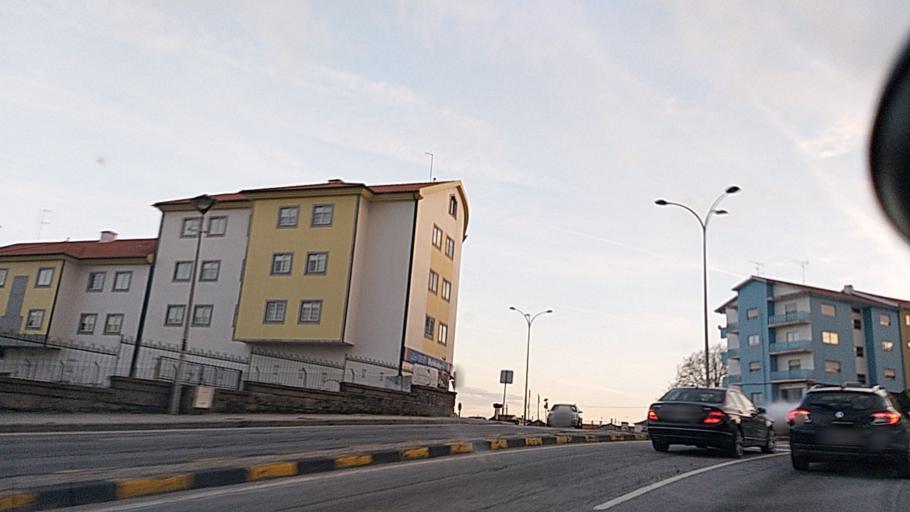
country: PT
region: Guarda
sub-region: Guarda
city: Guarda
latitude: 40.5451
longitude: -7.2529
